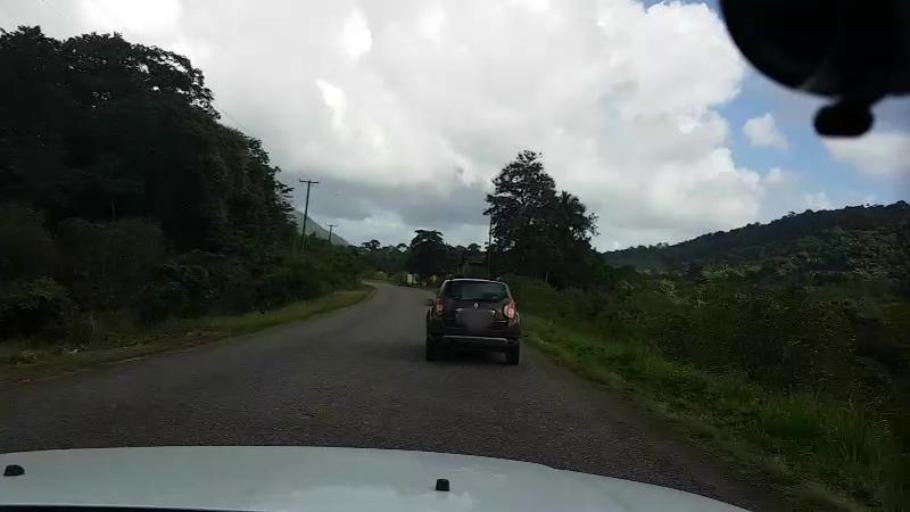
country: BZ
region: Stann Creek
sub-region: Dangriga
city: Dangriga
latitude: 16.9988
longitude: -88.4291
